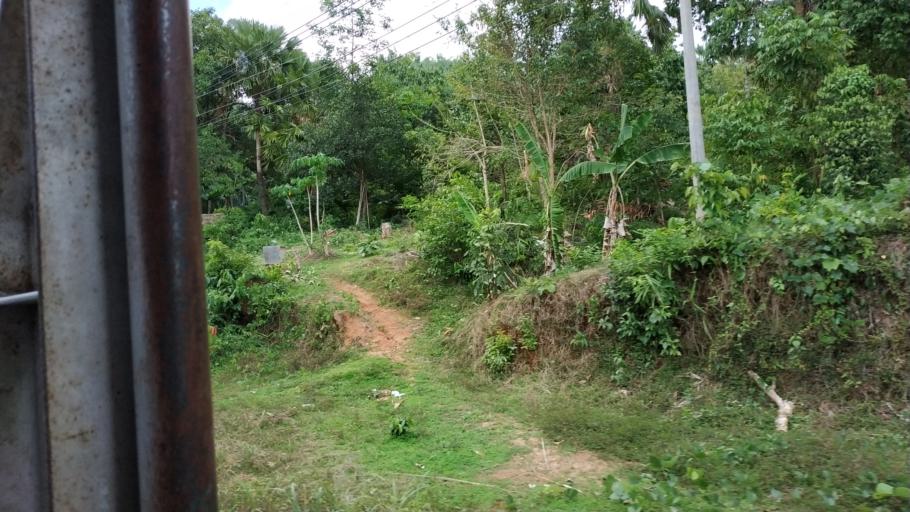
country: MM
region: Mon
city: Kyaikto
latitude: 17.4205
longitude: 97.0719
